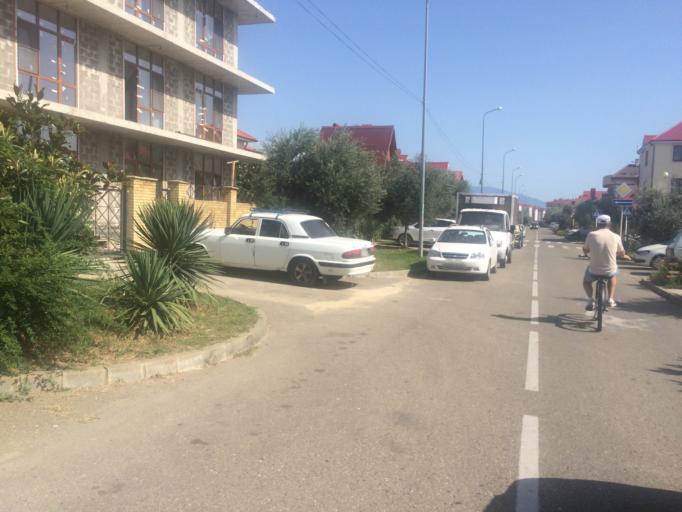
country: RU
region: Krasnodarskiy
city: Adler
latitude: 43.3994
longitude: 39.9691
